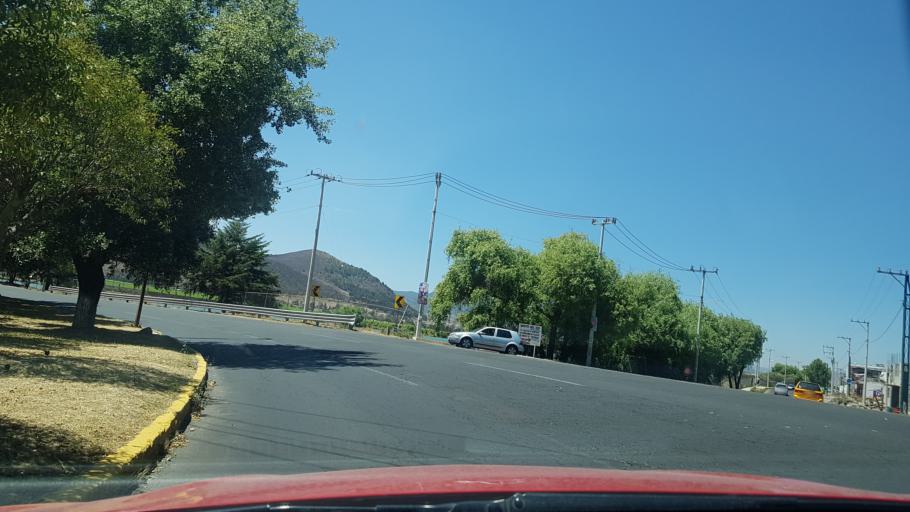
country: MX
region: Mexico
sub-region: Atlacomulco
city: Santa Cruz Bombatevi
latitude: 19.7992
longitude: -99.8902
